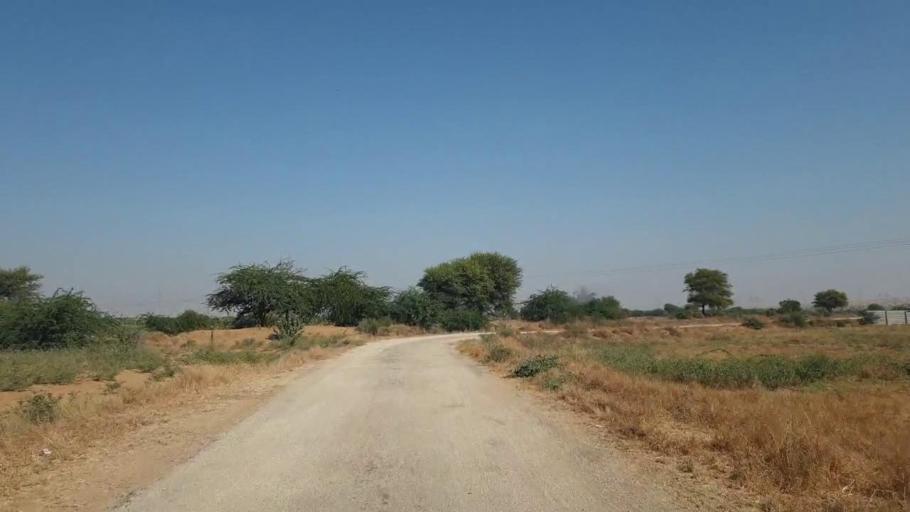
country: PK
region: Sindh
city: Gharo
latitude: 25.1824
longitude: 67.7350
